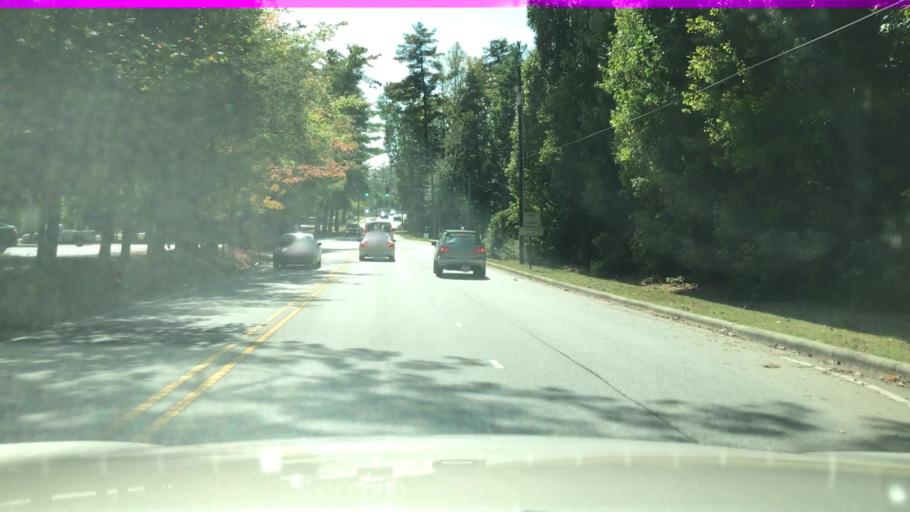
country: US
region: North Carolina
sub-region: Buncombe County
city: Royal Pines
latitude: 35.4899
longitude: -82.5376
